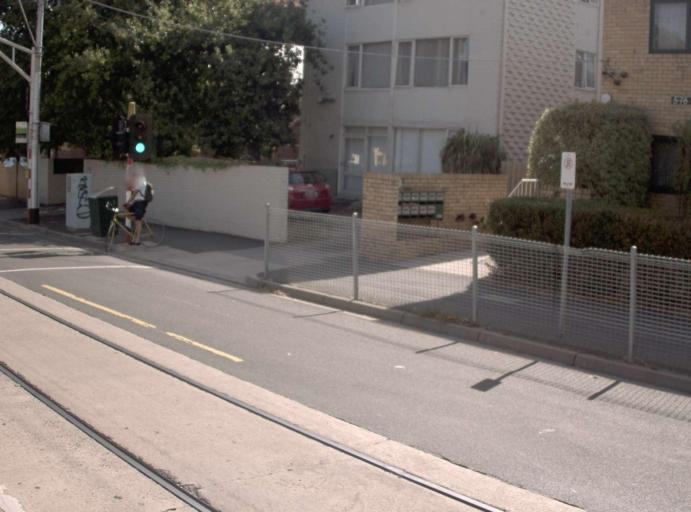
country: AU
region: Victoria
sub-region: Boroondara
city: Hawthorn East
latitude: -37.8262
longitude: 145.0347
